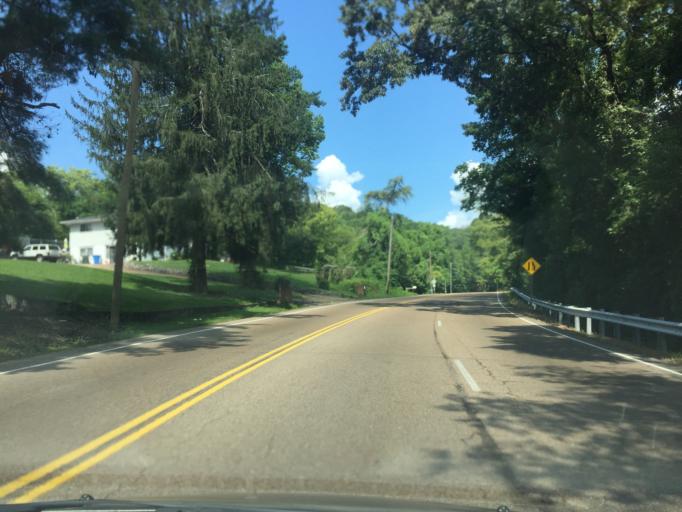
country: US
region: Tennessee
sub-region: Hamilton County
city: East Chattanooga
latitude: 35.0478
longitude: -85.2464
